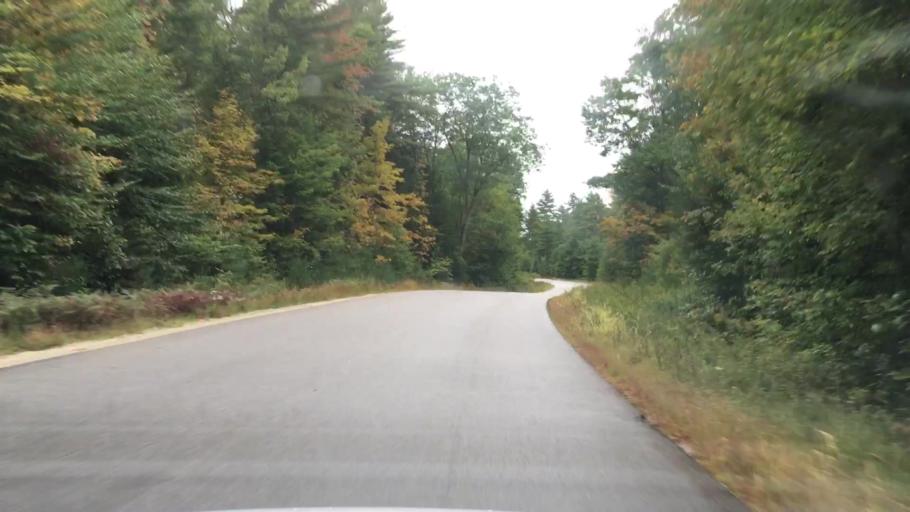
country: US
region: Maine
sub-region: Cumberland County
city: Harrison
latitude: 44.0224
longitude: -70.5891
